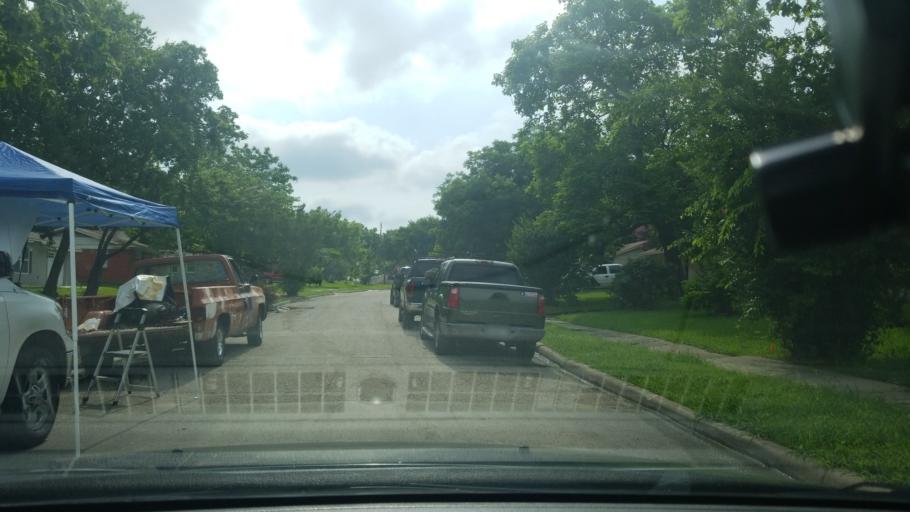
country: US
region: Texas
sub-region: Dallas County
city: Mesquite
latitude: 32.7581
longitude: -96.6237
